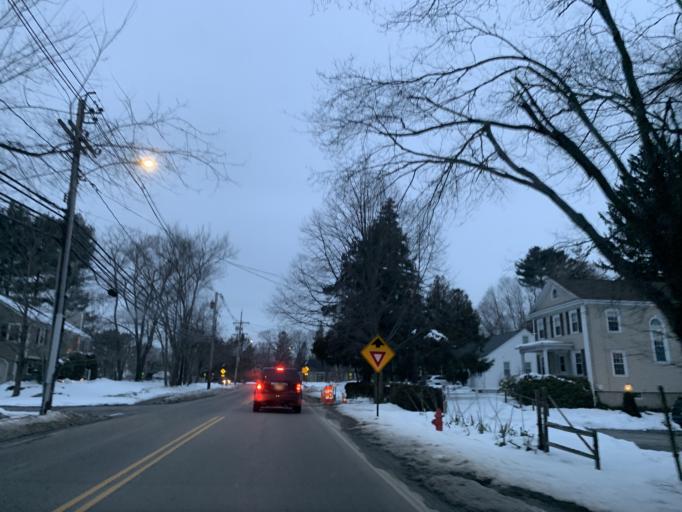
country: US
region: Massachusetts
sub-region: Norfolk County
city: Canton
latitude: 42.1502
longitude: -71.1265
